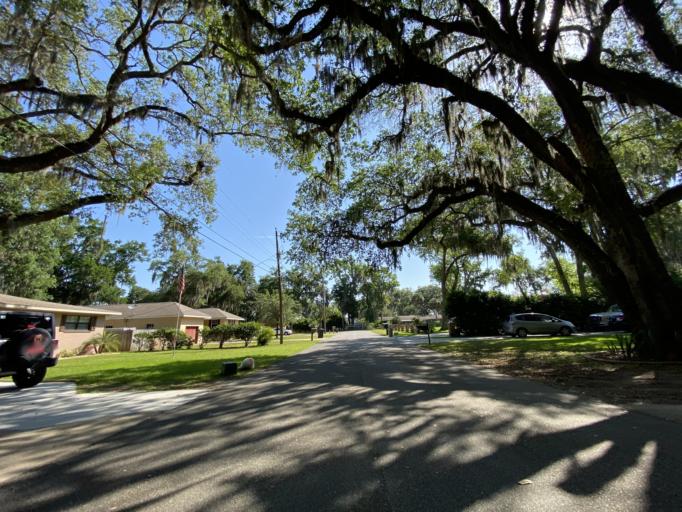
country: US
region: Florida
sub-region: Volusia County
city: South Daytona
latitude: 29.1680
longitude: -81.0157
